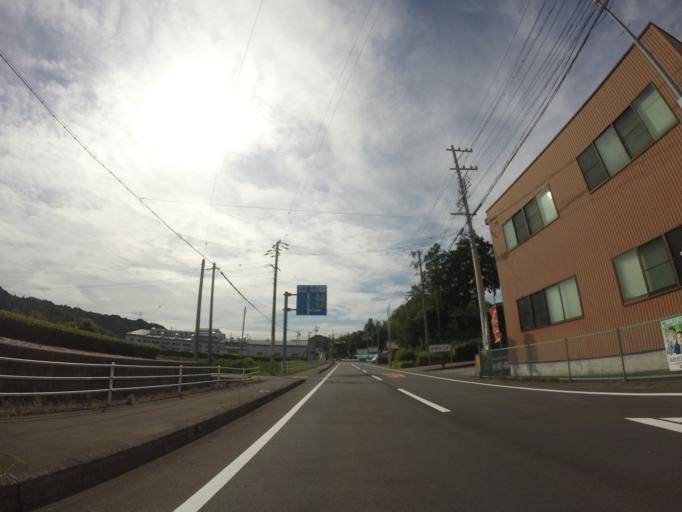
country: JP
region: Shizuoka
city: Shimada
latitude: 34.7661
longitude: 138.1916
